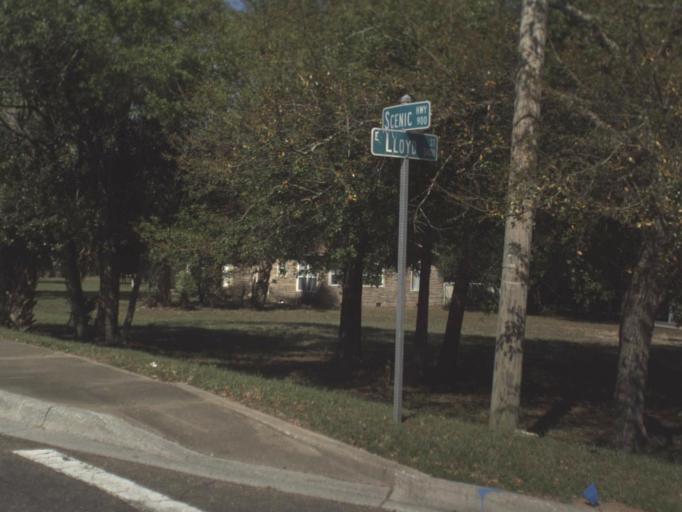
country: US
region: Florida
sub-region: Escambia County
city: East Pensacola Heights
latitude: 30.4298
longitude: -87.1759
